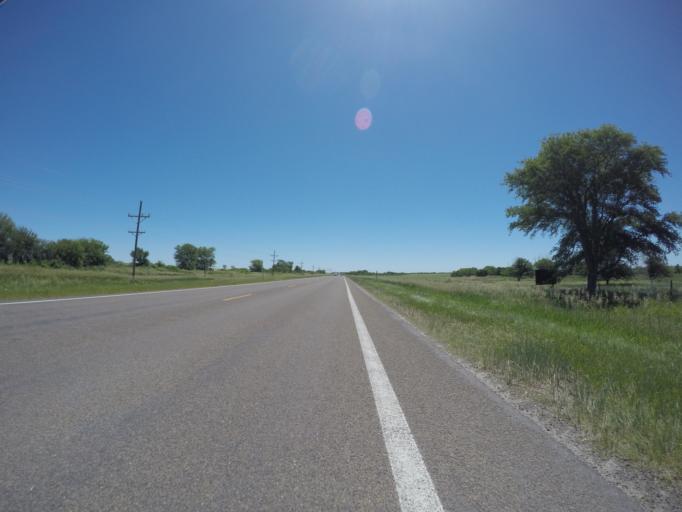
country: US
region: Kansas
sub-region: Phillips County
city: Phillipsburg
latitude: 39.8214
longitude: -99.5421
